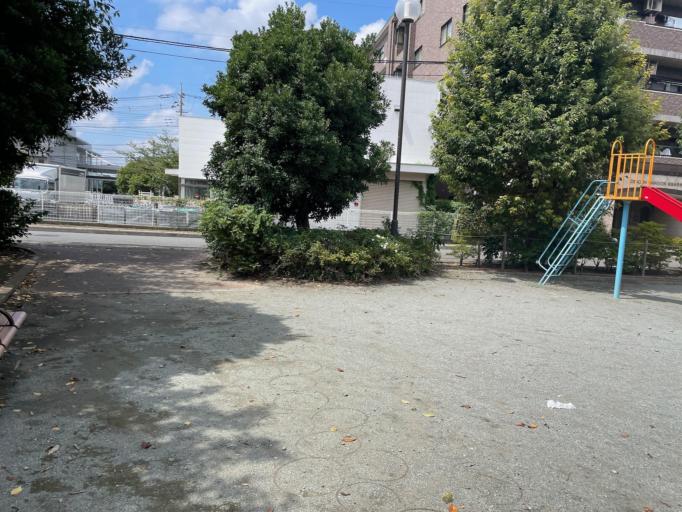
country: JP
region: Saitama
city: Wako
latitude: 35.7930
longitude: 139.6395
